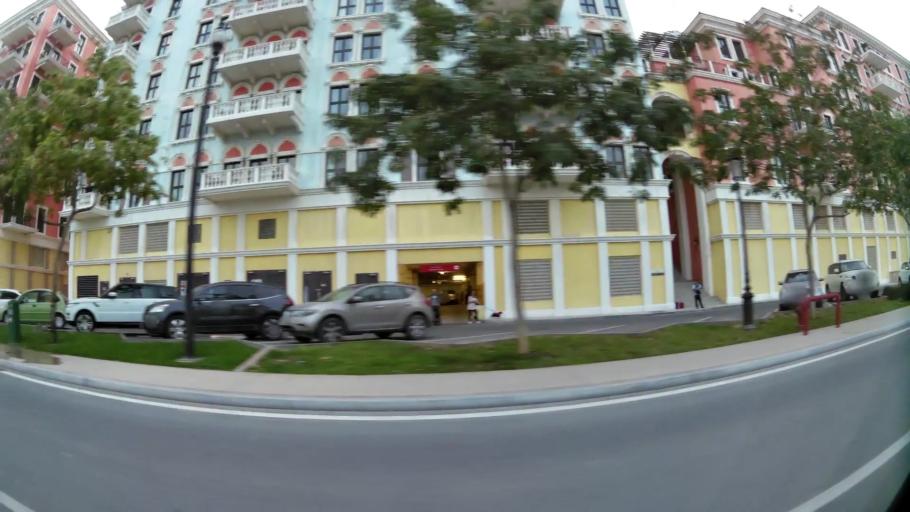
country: QA
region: Baladiyat ad Dawhah
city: Doha
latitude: 25.3763
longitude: 51.5460
